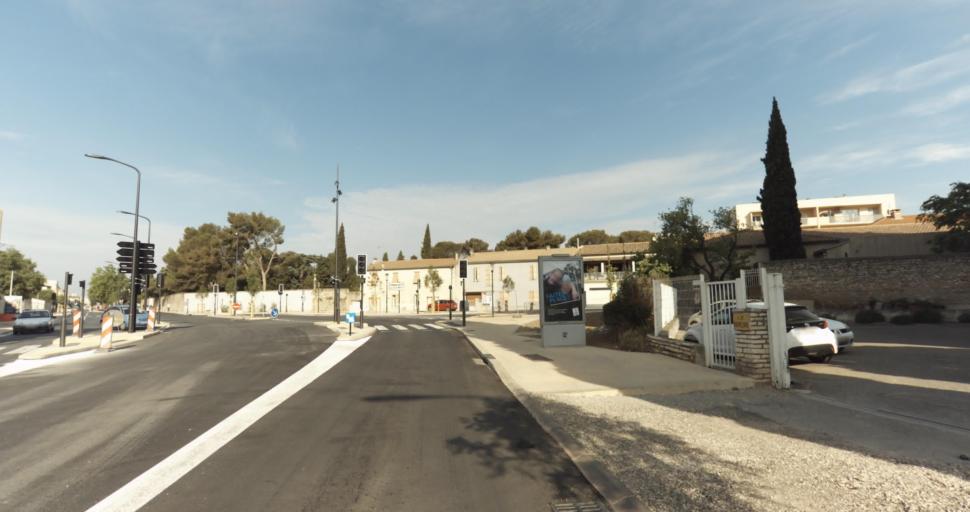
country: FR
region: Languedoc-Roussillon
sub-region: Departement du Gard
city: Nimes
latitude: 43.8429
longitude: 4.3821
